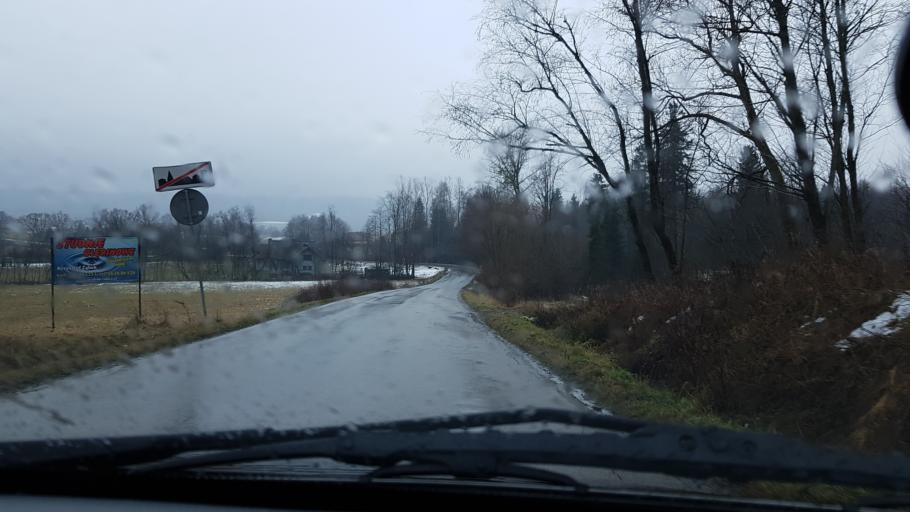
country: PL
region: Lesser Poland Voivodeship
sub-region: Powiat nowotarski
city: Spytkowice
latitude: 49.5974
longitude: 19.8387
